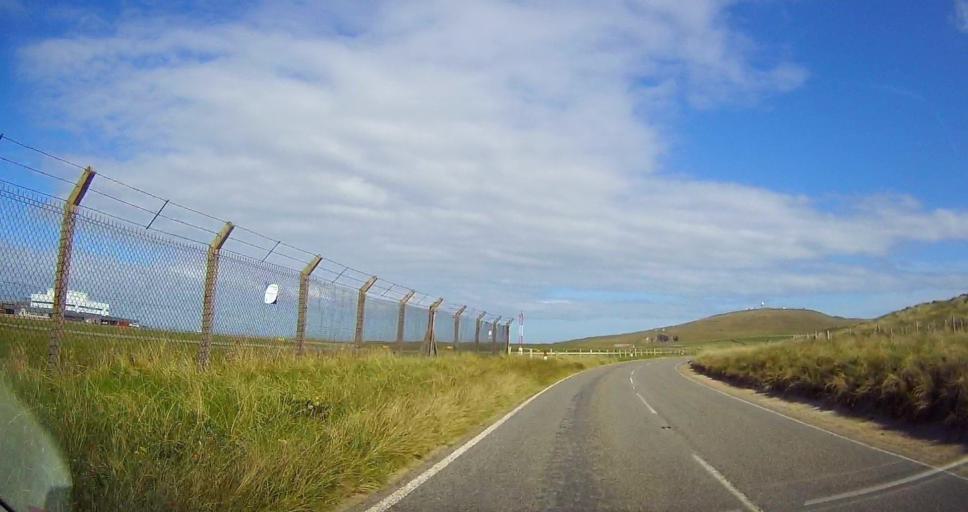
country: GB
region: Scotland
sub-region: Shetland Islands
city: Sandwick
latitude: 59.8761
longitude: -1.2954
